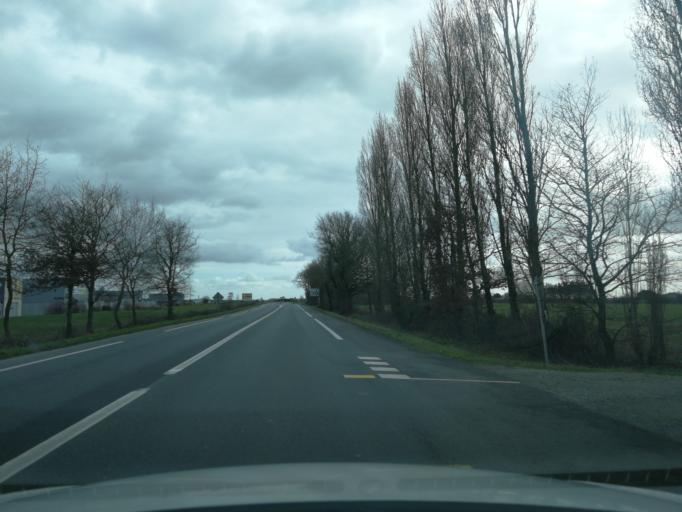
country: FR
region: Pays de la Loire
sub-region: Departement de la Vendee
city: Chavagnes-en-Paillers
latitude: 46.9169
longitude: -1.2441
